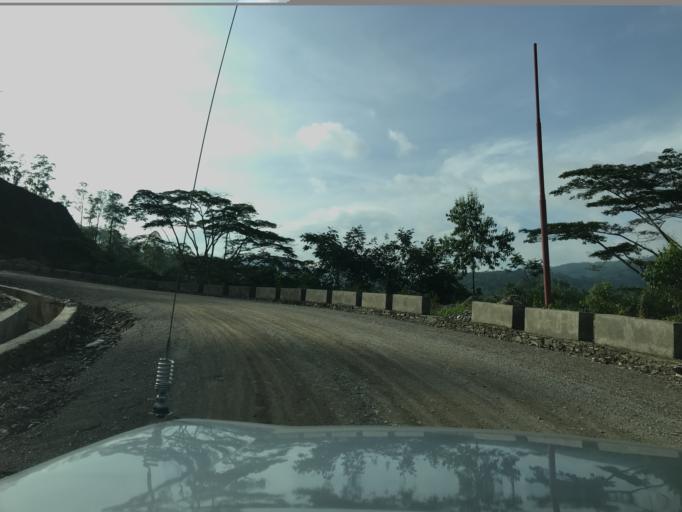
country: TL
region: Aileu
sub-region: Aileu Villa
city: Aileu
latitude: -8.6568
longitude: 125.5270
